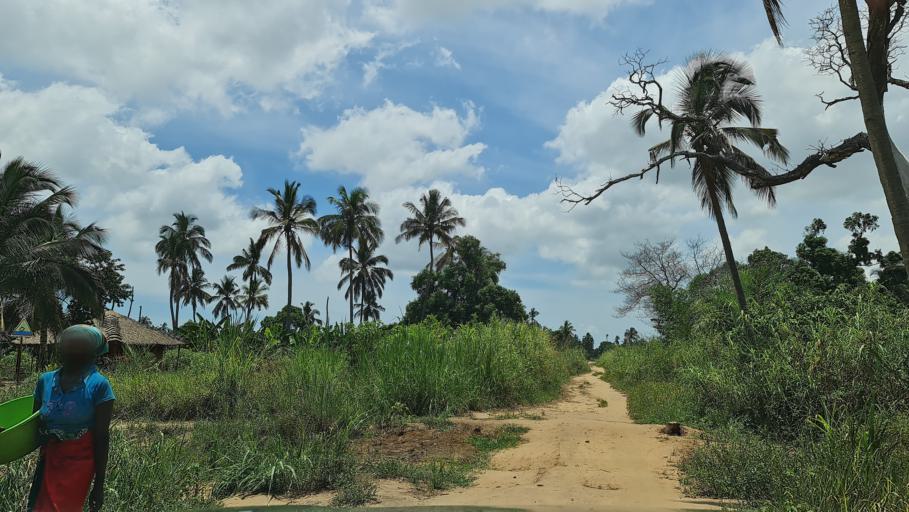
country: MZ
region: Zambezia
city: Quelimane
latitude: -17.5725
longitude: 37.3737
